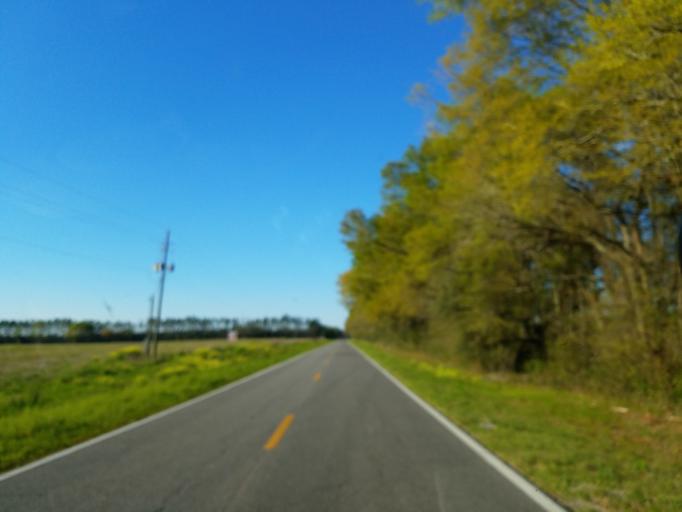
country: US
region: Florida
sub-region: Suwannee County
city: Wellborn
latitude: 30.1056
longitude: -82.8786
